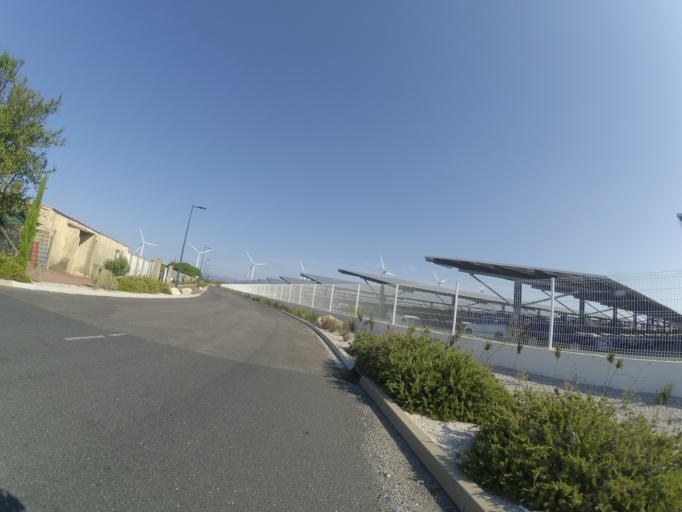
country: FR
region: Languedoc-Roussillon
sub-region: Departement des Pyrenees-Orientales
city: Rivesaltes
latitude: 42.7989
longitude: 2.8873
